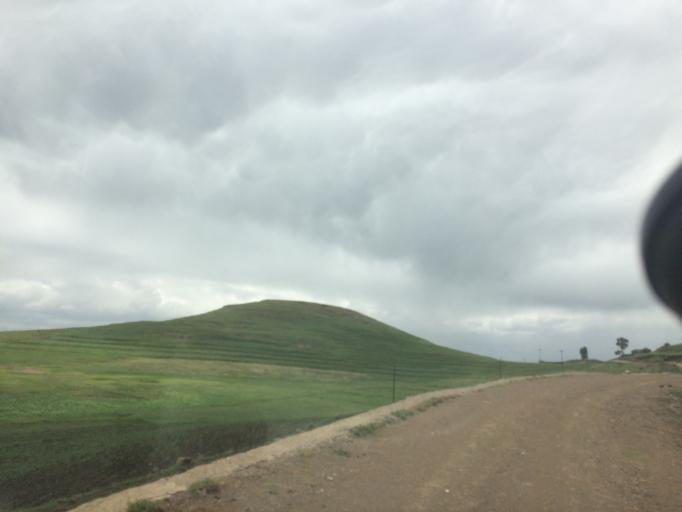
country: LS
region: Maseru
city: Nako
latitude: -29.8443
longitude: 28.0250
